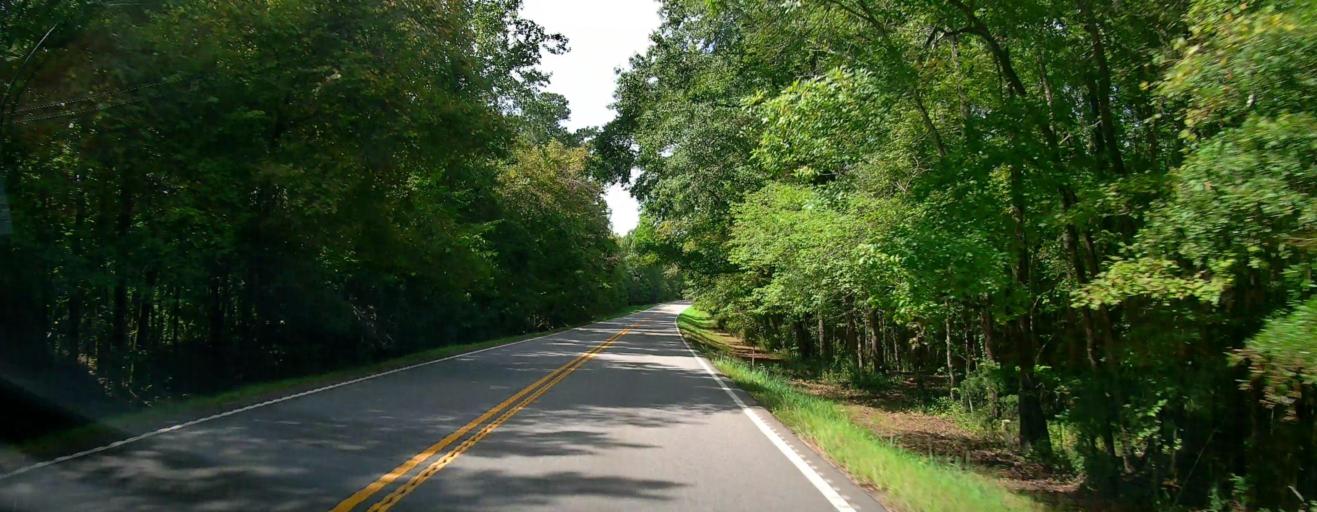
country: US
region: Georgia
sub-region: Talbot County
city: Talbotton
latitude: 32.6452
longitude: -84.5030
